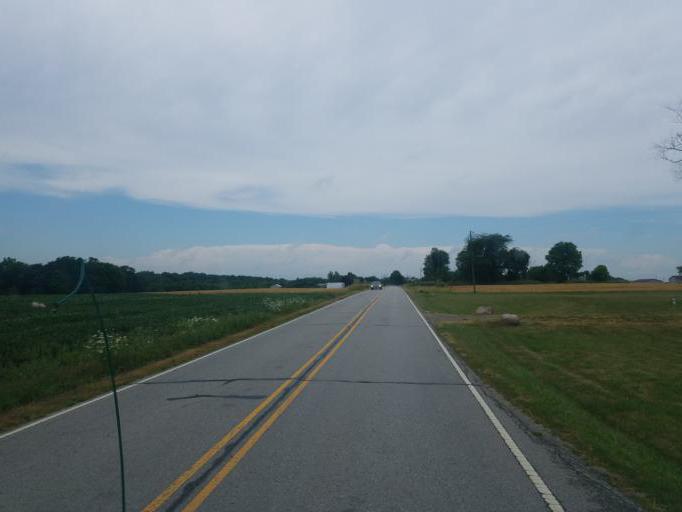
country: US
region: Indiana
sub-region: DeKalb County
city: Butler
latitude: 41.3866
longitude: -84.8257
